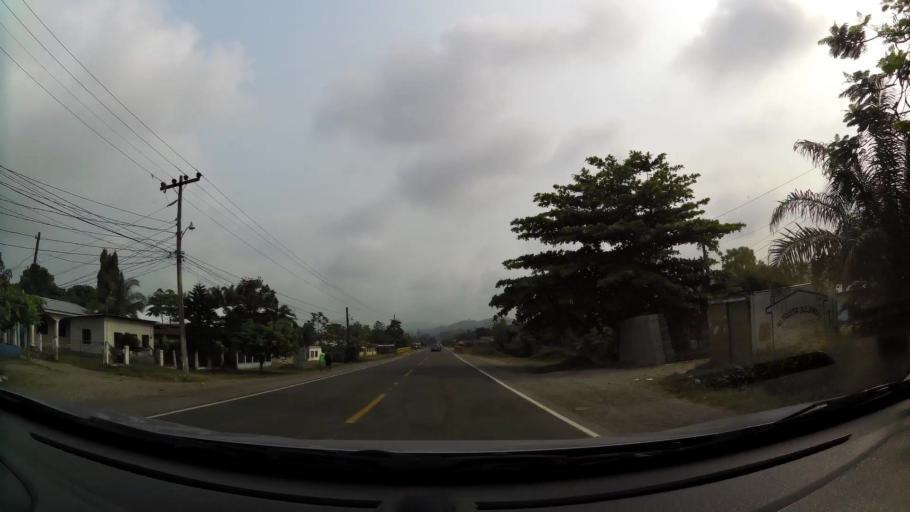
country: HN
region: Yoro
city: Toyos
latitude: 15.5406
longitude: -87.6524
